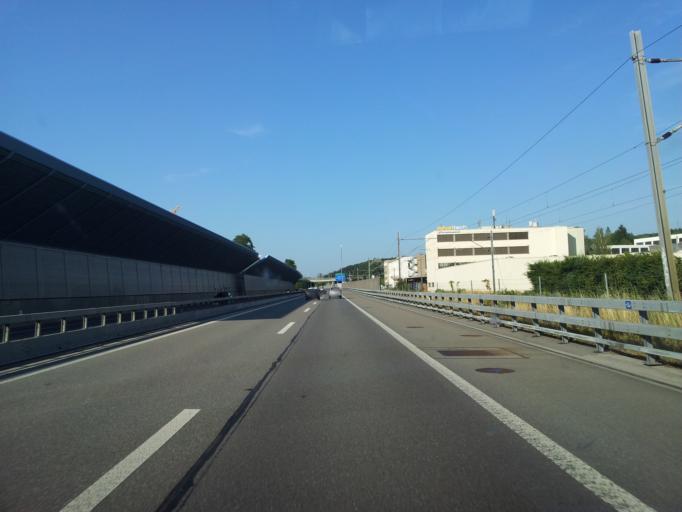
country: CH
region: Bern
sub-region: Bern-Mittelland District
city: Koniz
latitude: 46.9236
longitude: 7.3725
